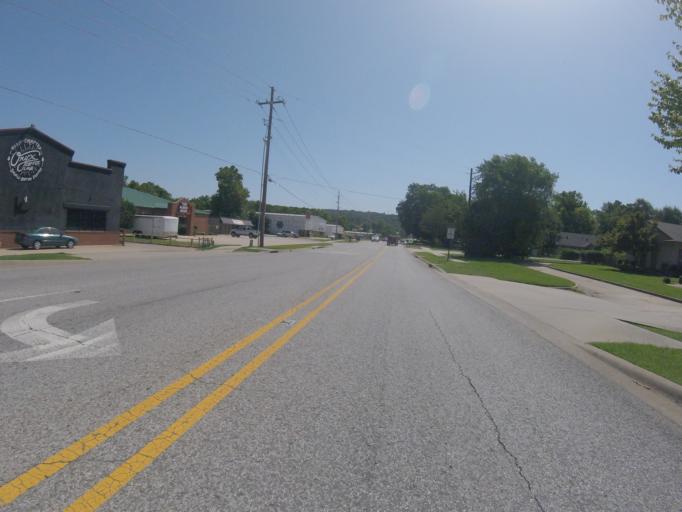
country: US
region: Arkansas
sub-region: Washington County
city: Fayetteville
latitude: 36.0953
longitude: -94.1603
